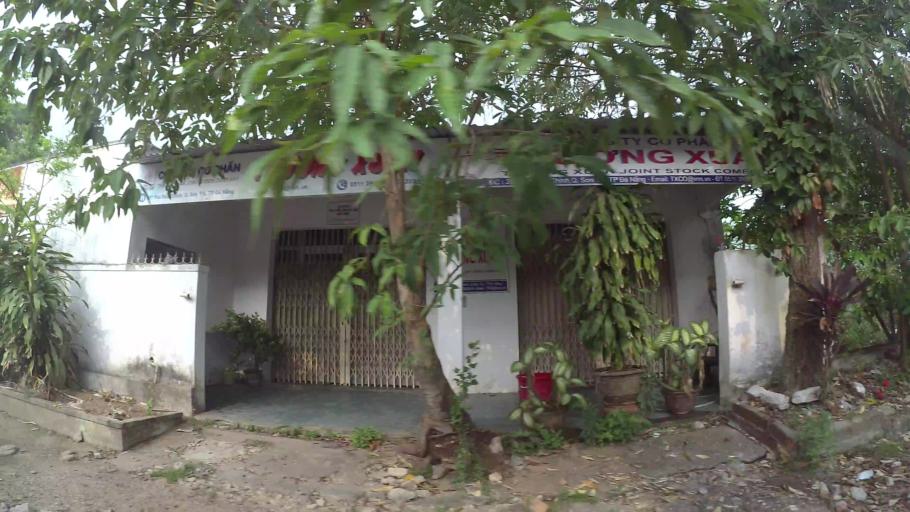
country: VN
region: Da Nang
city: Son Tra
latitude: 16.0796
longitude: 108.2392
